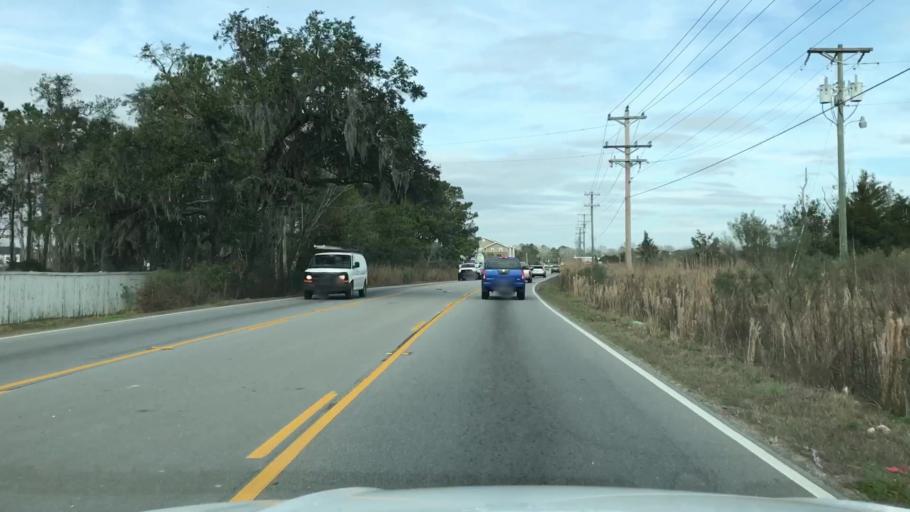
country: US
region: South Carolina
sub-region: Charleston County
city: Shell Point
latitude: 32.7965
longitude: -80.1084
